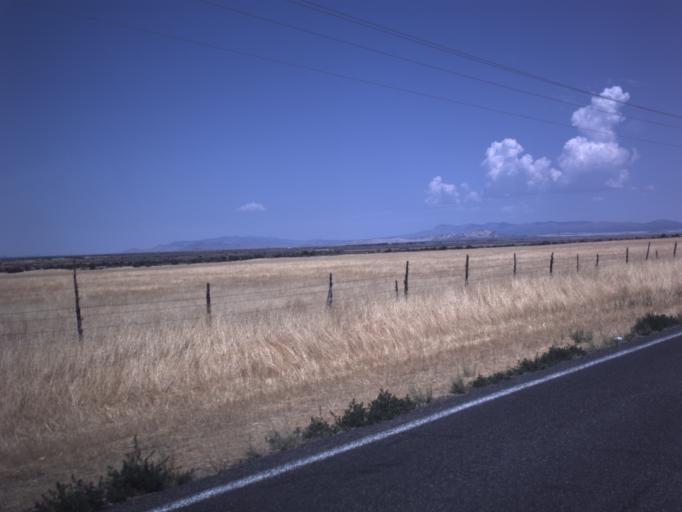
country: US
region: Utah
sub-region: Millard County
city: Delta
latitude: 39.4231
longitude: -112.3274
